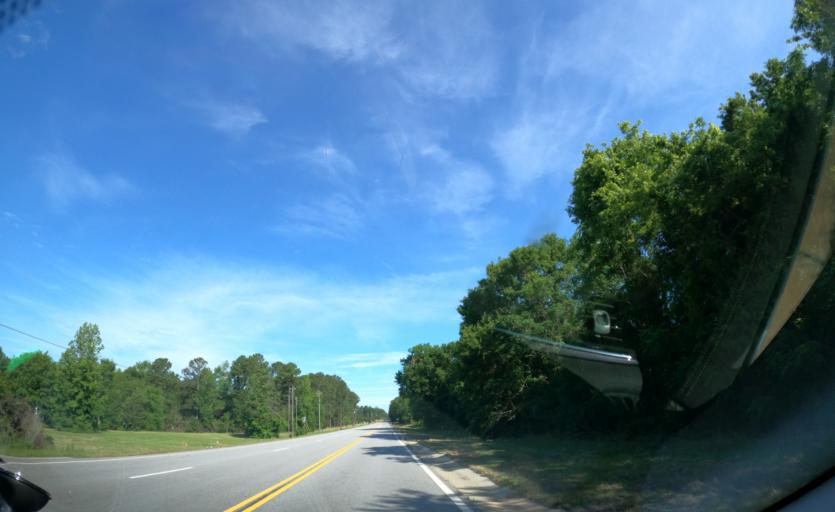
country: US
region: Georgia
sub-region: Columbia County
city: Appling
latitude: 33.6552
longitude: -82.3268
